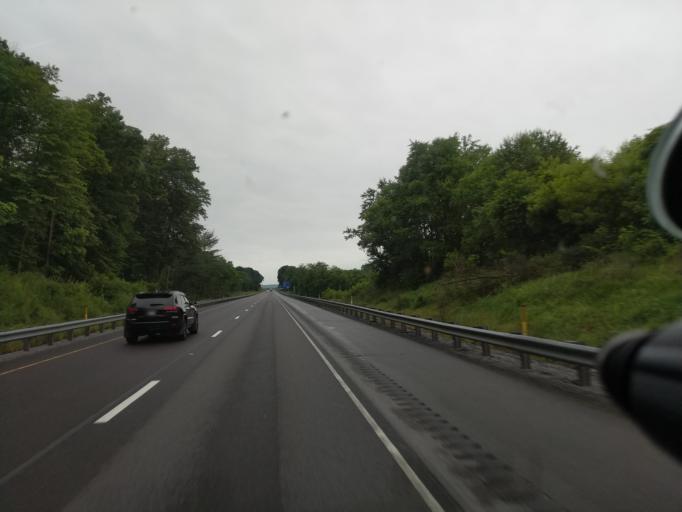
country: US
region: Pennsylvania
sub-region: Clinton County
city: Mill Hall
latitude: 41.0390
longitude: -77.4967
